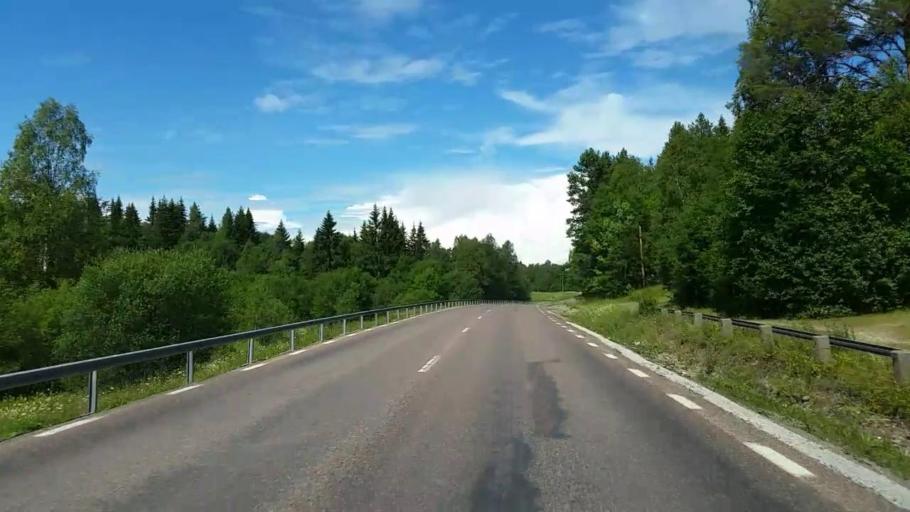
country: SE
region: Dalarna
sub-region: Rattviks Kommun
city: Raettvik
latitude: 61.0218
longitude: 15.2100
